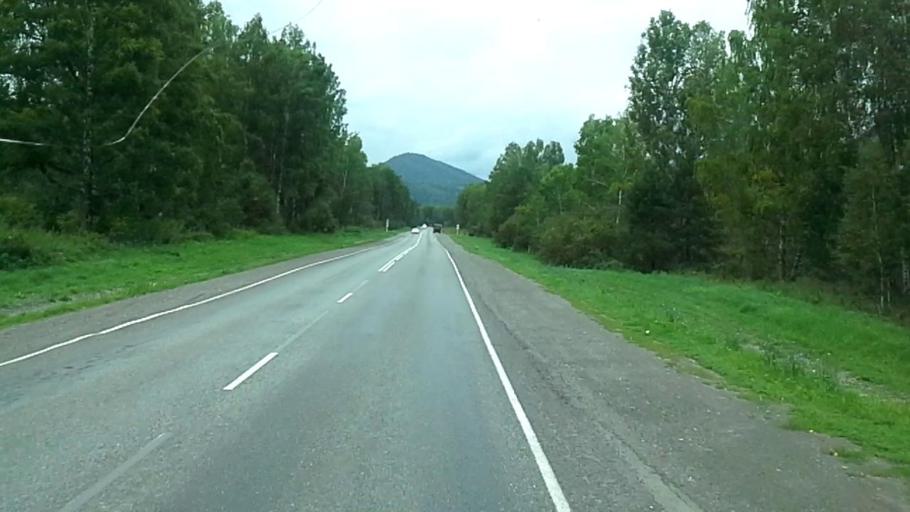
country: RU
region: Altay
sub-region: Mayminskiy Rayon
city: Manzherok
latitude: 51.8543
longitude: 85.7452
